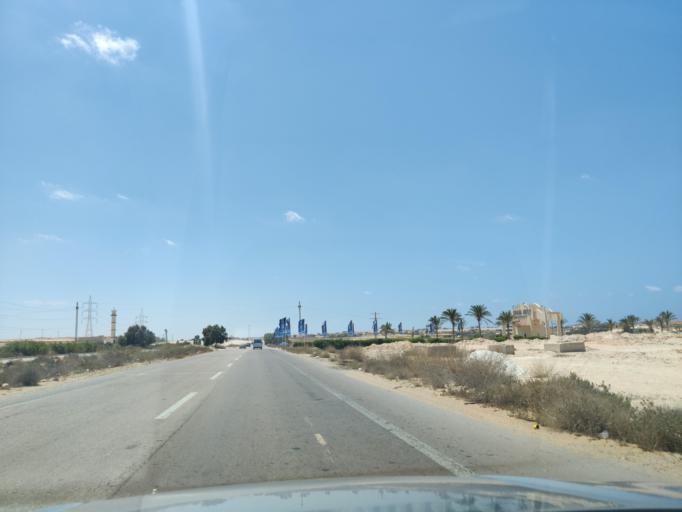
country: EG
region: Muhafazat Matruh
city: Al `Alamayn
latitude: 31.0692
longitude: 28.1647
